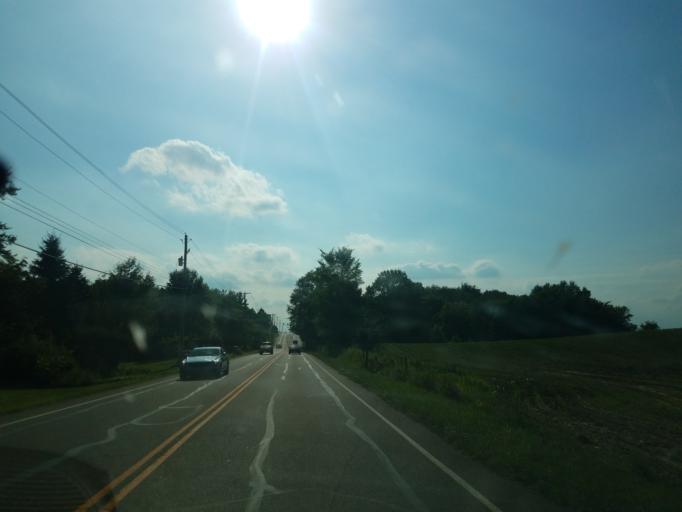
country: US
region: Ohio
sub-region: Stark County
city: Canal Fulton
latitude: 40.8810
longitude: -81.5397
